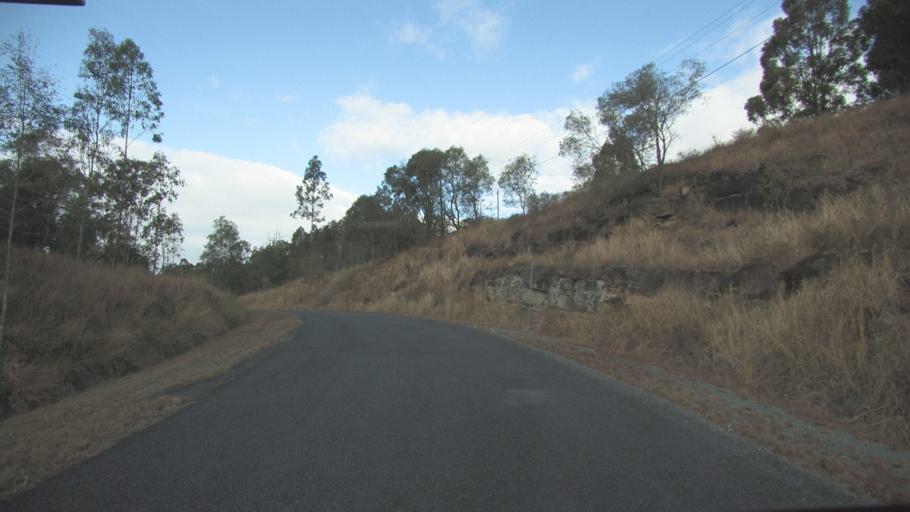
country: AU
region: Queensland
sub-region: Logan
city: Cedar Vale
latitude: -27.9042
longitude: 153.0664
